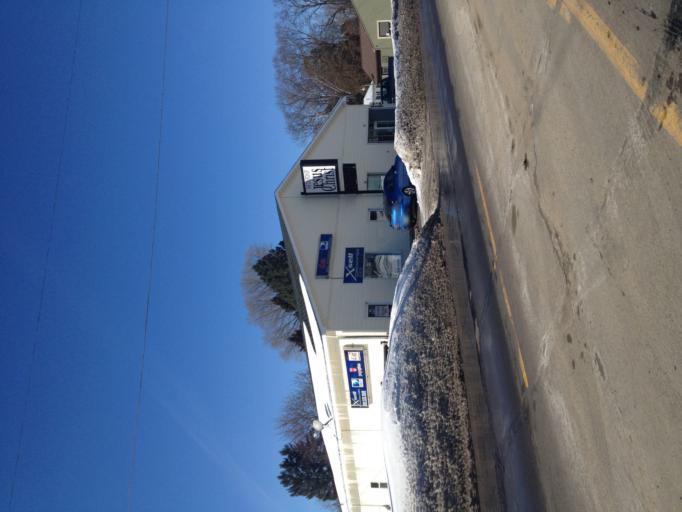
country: US
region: Michigan
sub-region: Clare County
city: Harrison
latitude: 44.0157
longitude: -84.7994
